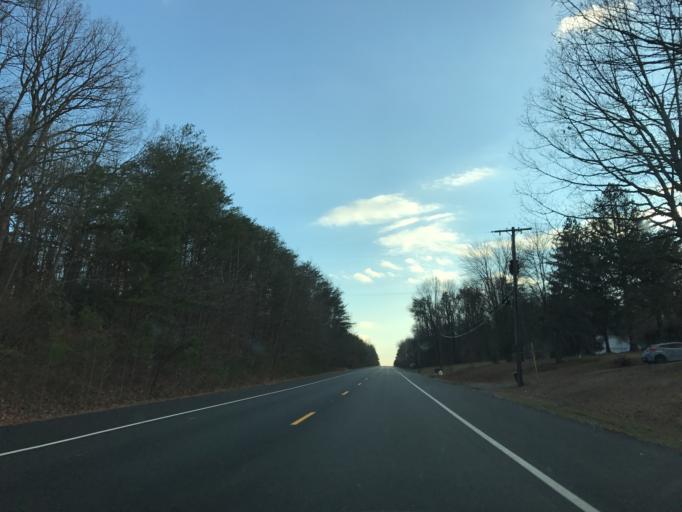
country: US
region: Maryland
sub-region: Cecil County
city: North East
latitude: 39.5735
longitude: -75.9449
